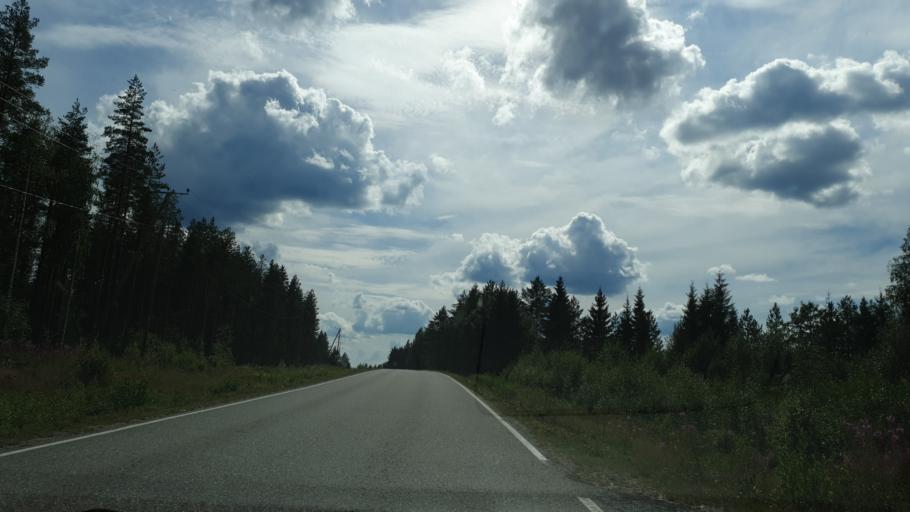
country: FI
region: Kainuu
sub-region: Kajaani
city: Sotkamo
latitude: 64.1950
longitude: 28.4633
